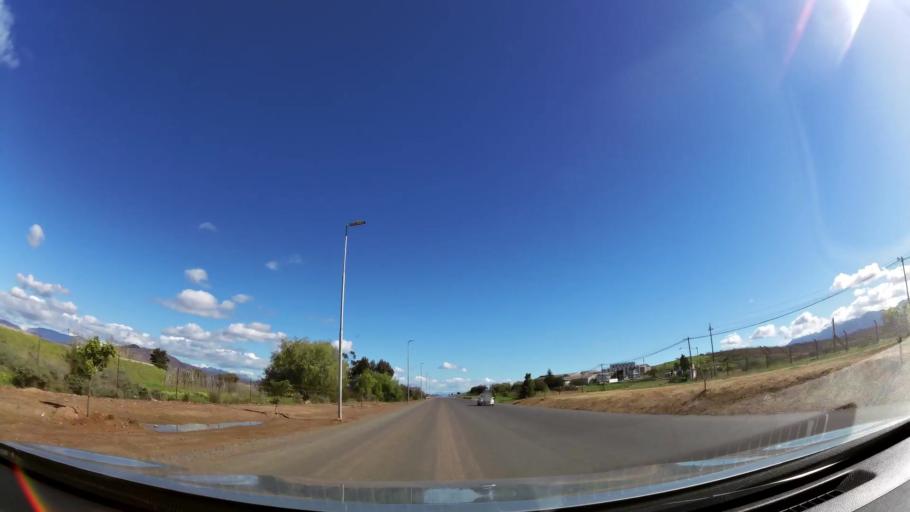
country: ZA
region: Western Cape
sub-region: Cape Winelands District Municipality
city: Ashton
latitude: -33.8373
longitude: 20.0351
